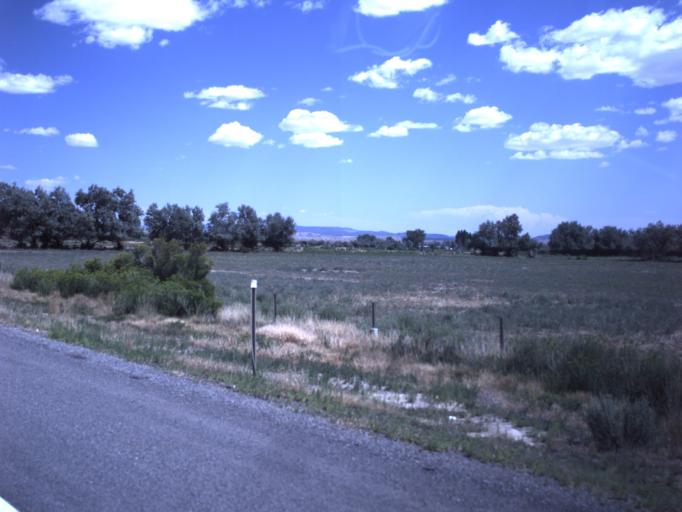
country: US
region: Utah
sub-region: Emery County
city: Huntington
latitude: 39.3392
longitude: -110.9523
